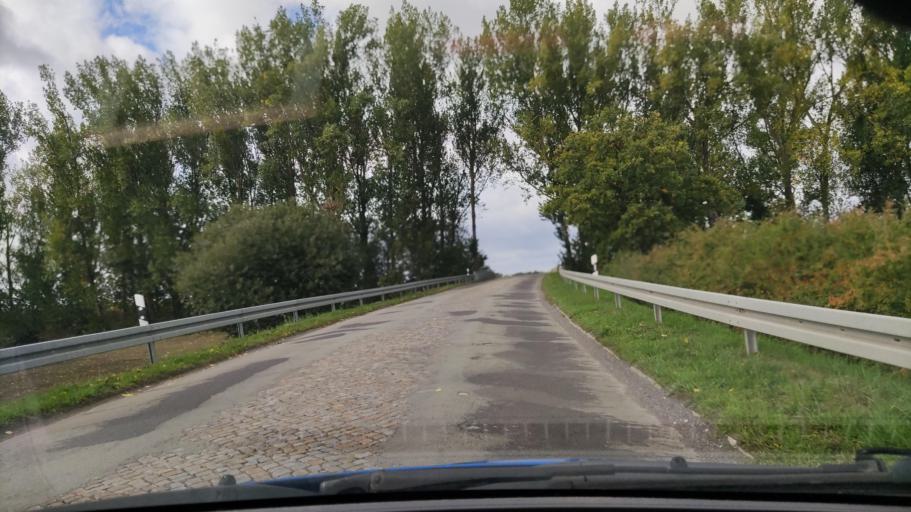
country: DE
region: Saxony-Anhalt
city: Salzwedel
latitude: 52.8532
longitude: 11.2014
